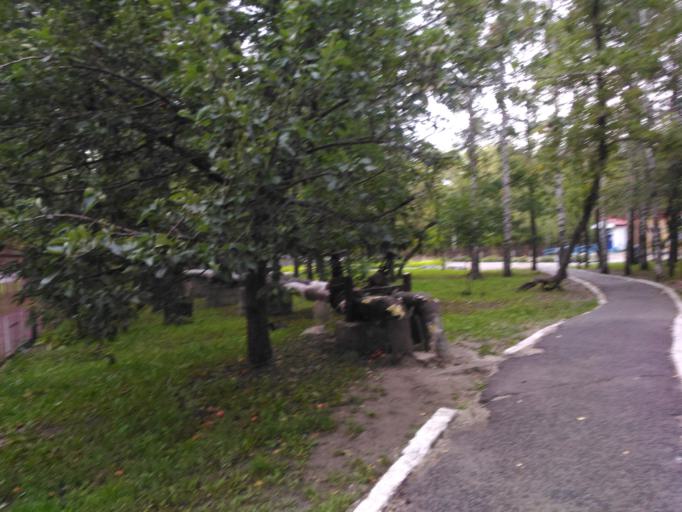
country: RU
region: Ulyanovsk
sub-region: Ulyanovskiy Rayon
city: Ulyanovsk
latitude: 54.2646
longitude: 48.3350
